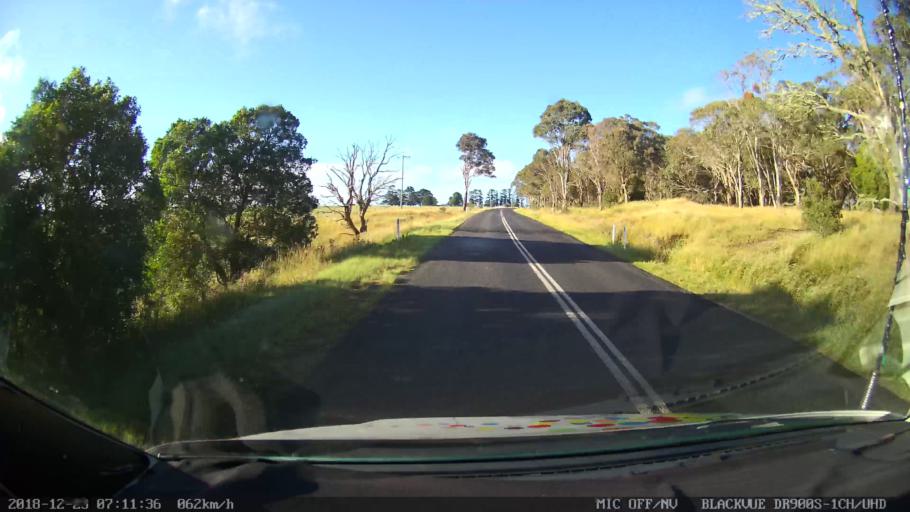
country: AU
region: New South Wales
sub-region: Bellingen
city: Dorrigo
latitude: -30.4068
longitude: 152.3460
